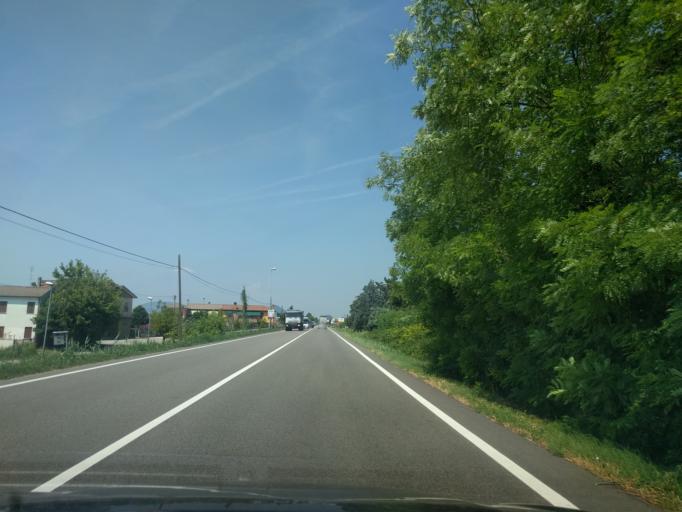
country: IT
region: Veneto
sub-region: Provincia di Padova
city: Solesino
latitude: 45.1620
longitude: 11.7563
